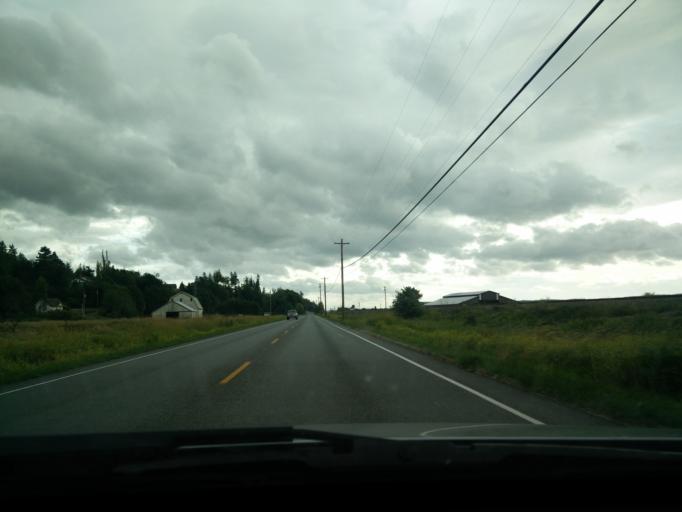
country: US
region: Washington
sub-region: Snohomish County
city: Stanwood
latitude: 48.2830
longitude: -122.3597
